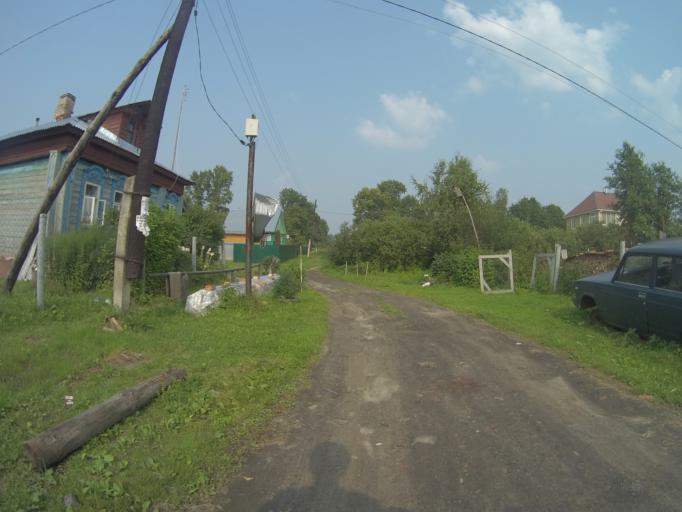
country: RU
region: Vladimir
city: Vorsha
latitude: 56.0126
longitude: 40.1278
